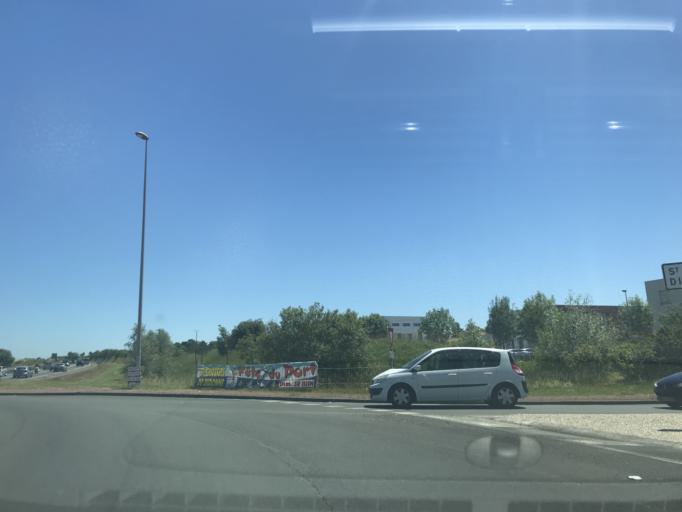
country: FR
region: Poitou-Charentes
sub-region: Departement de la Charente-Maritime
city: Saint-Georges-de-Didonne
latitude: 45.6163
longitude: -0.9883
